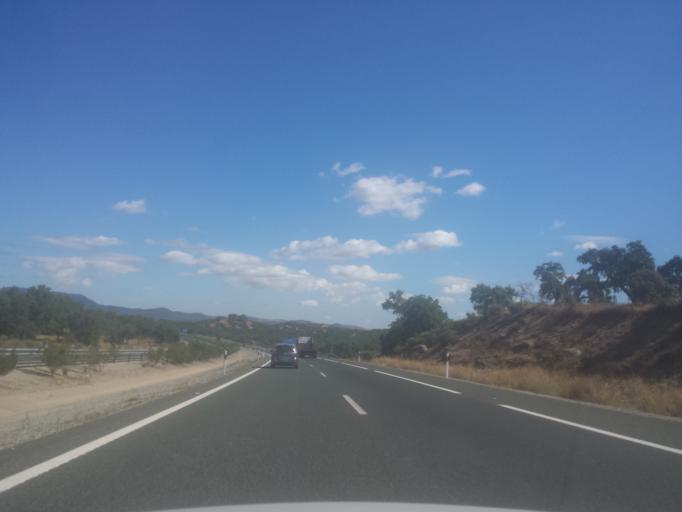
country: ES
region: Andalusia
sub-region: Provincia de Huelva
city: Santa Olalla del Cala
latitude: 37.9361
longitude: -6.2266
